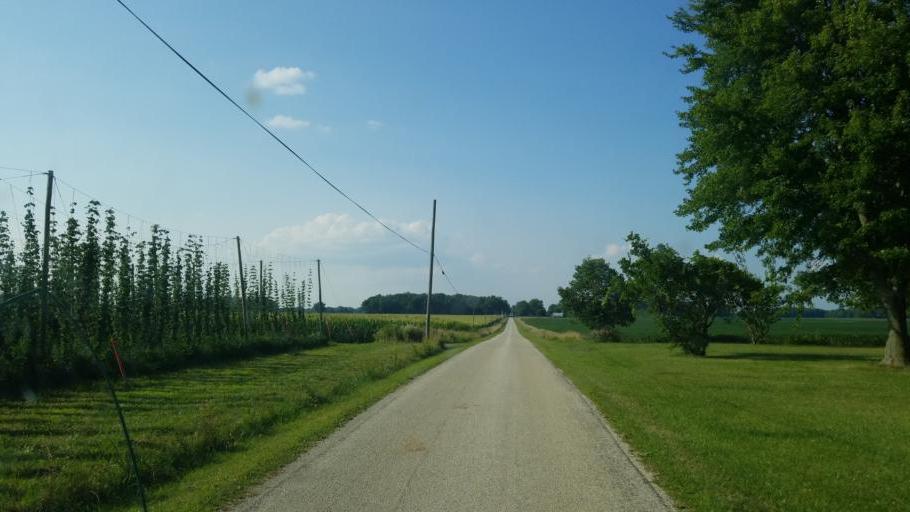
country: US
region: Ohio
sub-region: Crawford County
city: Bucyrus
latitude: 40.8843
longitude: -83.0740
